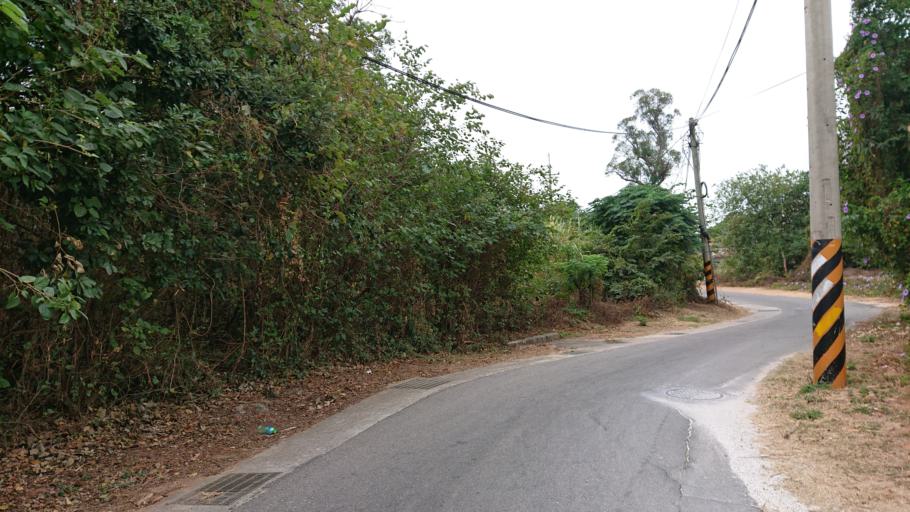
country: TW
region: Fukien
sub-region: Kinmen
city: Jincheng
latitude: 24.4456
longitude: 118.3135
